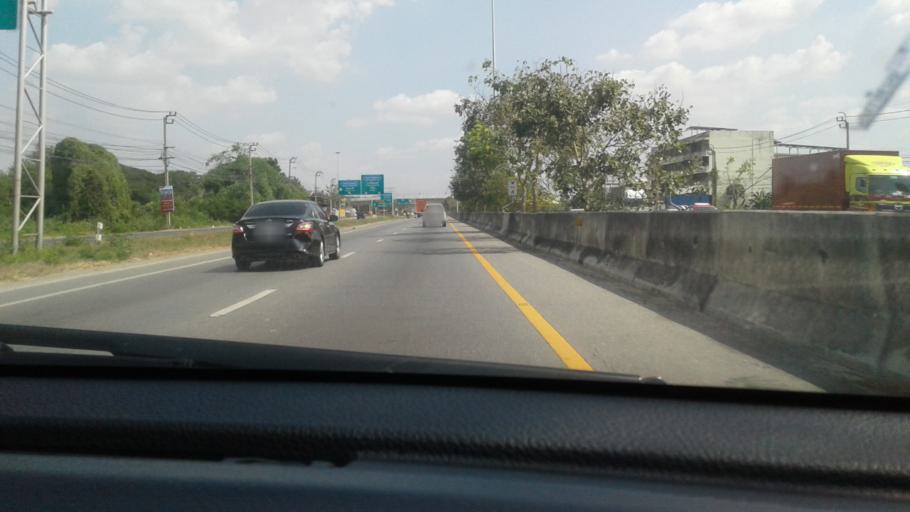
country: TH
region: Nonthaburi
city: Bang Bua Thong
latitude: 13.9498
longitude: 100.4532
